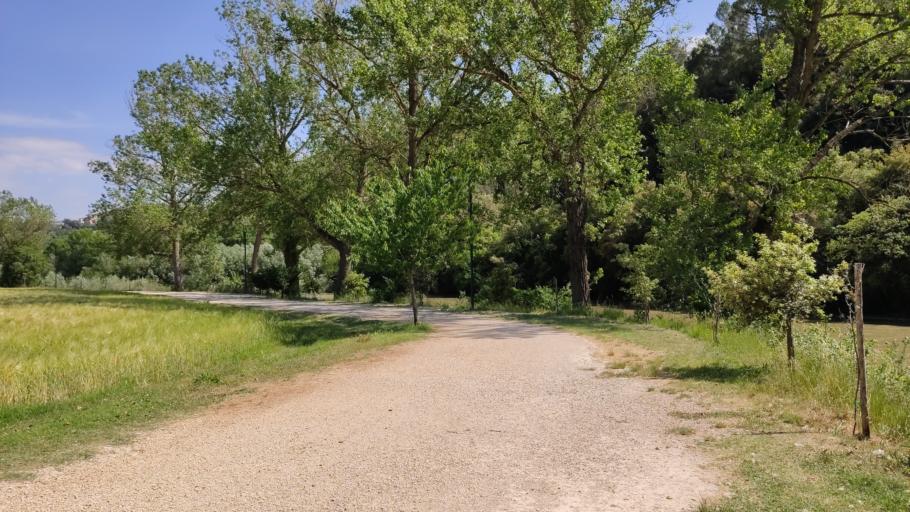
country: IT
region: Umbria
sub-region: Provincia di Terni
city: Amelia
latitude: 42.5638
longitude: 12.4121
